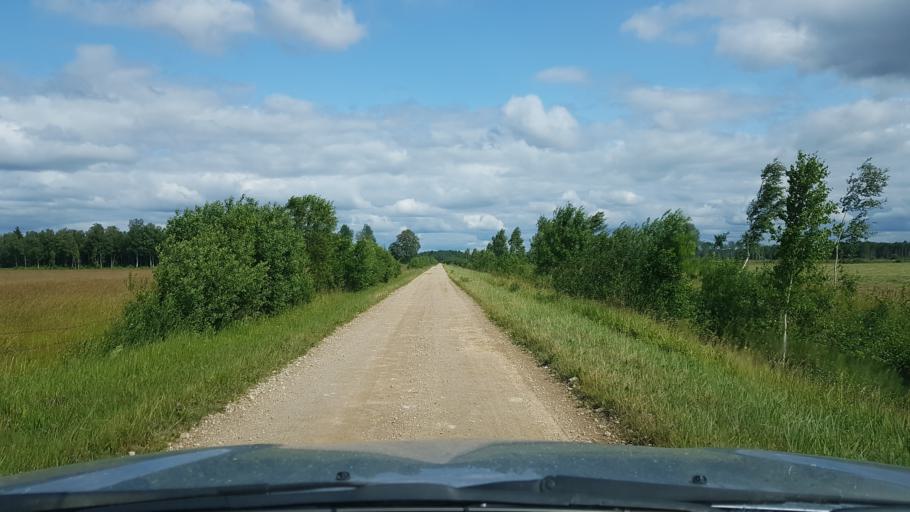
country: EE
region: Ida-Virumaa
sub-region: Sillamaee linn
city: Sillamae
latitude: 59.3703
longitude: 27.9066
